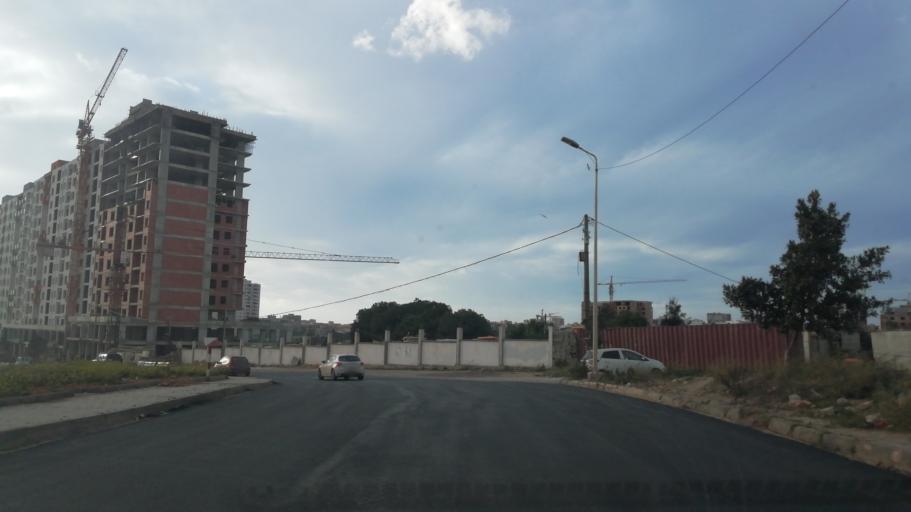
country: DZ
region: Oran
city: Bir el Djir
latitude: 35.7125
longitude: -0.5717
